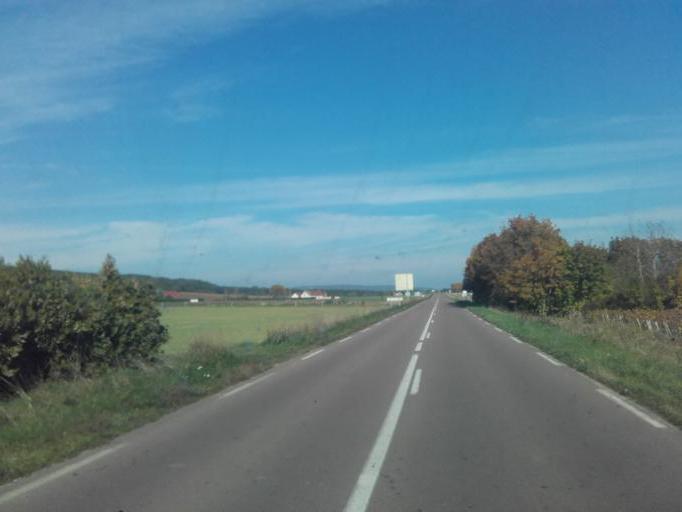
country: FR
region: Bourgogne
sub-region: Departement de Saone-et-Loire
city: Rully
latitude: 46.8803
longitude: 4.7524
